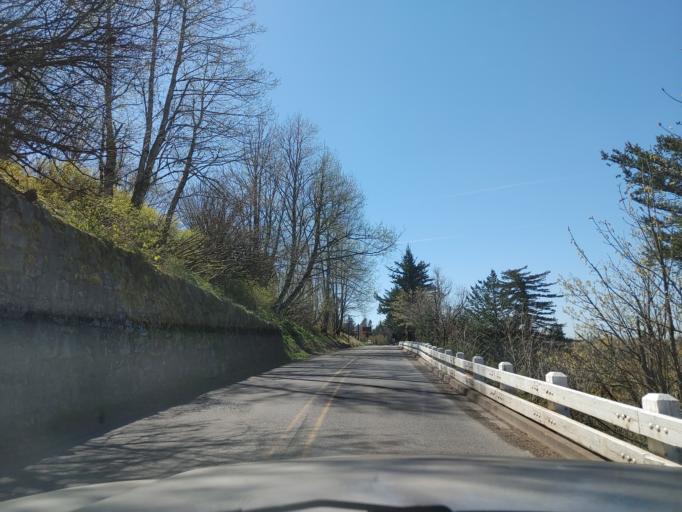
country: US
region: Washington
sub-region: Clark County
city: Washougal
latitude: 45.5321
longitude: -122.2510
